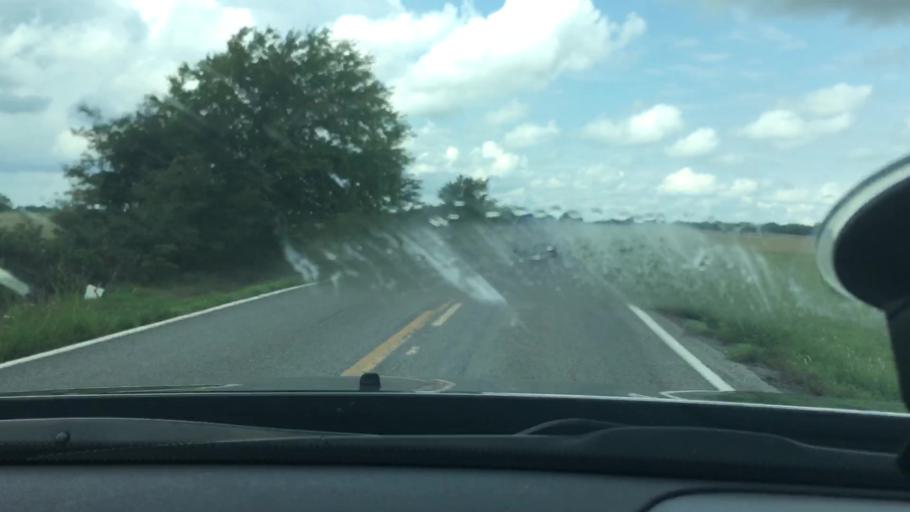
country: US
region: Oklahoma
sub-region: Johnston County
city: Tishomingo
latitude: 34.1955
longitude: -96.5378
